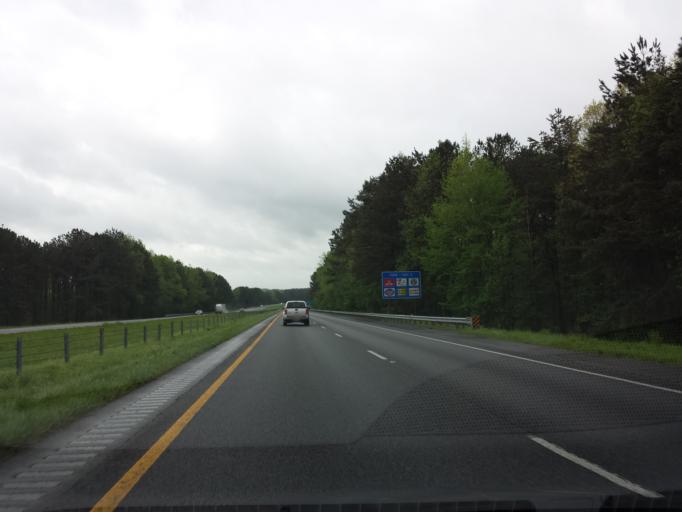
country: US
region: Georgia
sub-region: Cherokee County
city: Holly Springs
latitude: 34.1676
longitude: -84.5127
